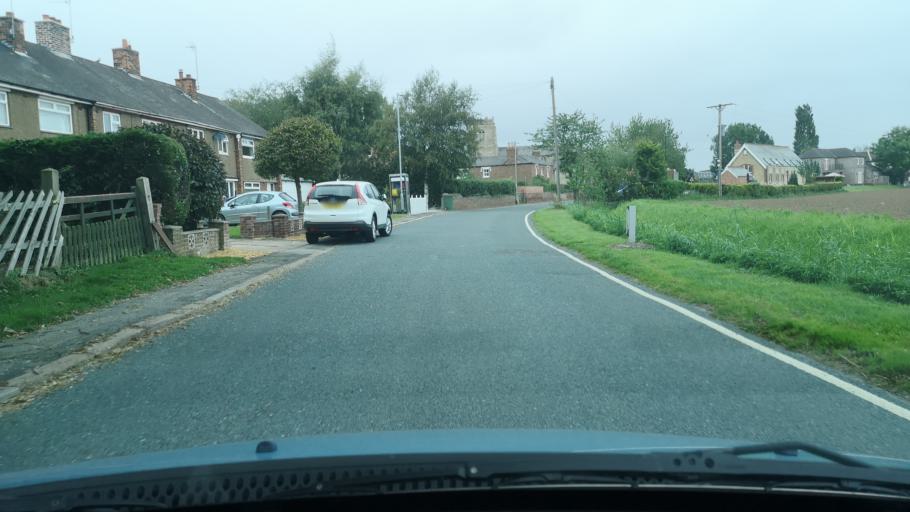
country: GB
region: England
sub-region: North Lincolnshire
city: Burton upon Stather
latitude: 53.6773
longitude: -0.7236
